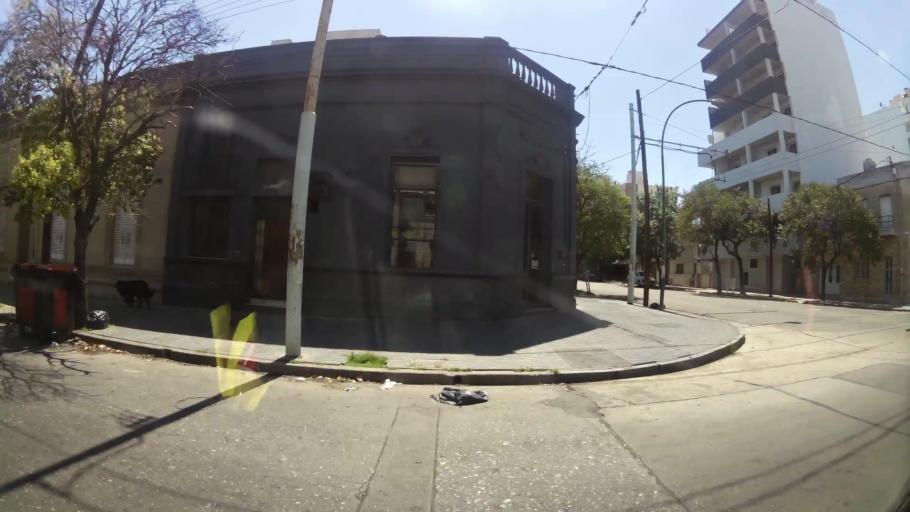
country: AR
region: Cordoba
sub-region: Departamento de Capital
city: Cordoba
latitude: -31.3995
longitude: -64.1860
